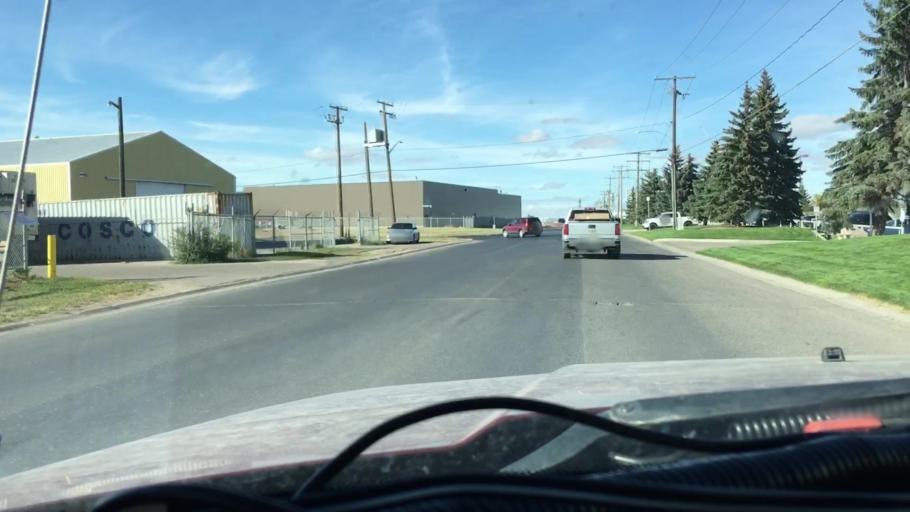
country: CA
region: Saskatchewan
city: Regina
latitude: 50.4744
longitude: -104.5615
